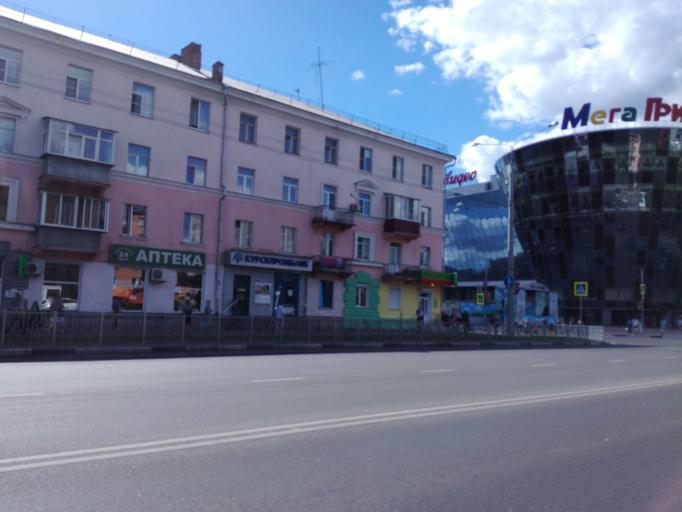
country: RU
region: Kursk
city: Kursk
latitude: 51.7603
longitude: 36.1863
